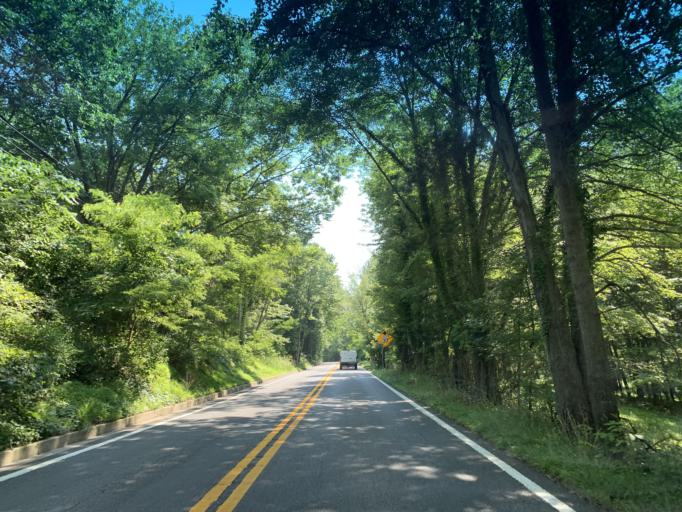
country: US
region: Maryland
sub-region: Montgomery County
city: Poolesville
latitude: 39.2255
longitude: -77.3730
